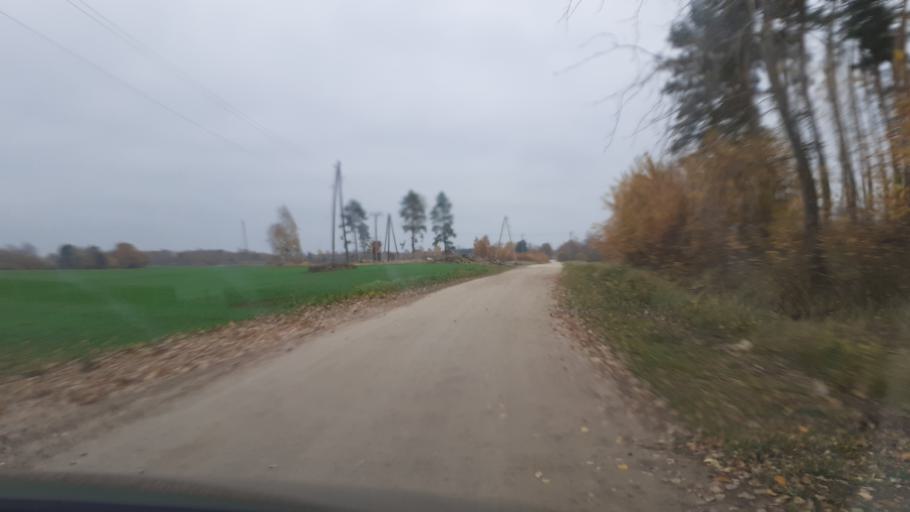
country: LV
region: Saldus Rajons
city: Saldus
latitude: 56.8666
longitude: 22.3112
